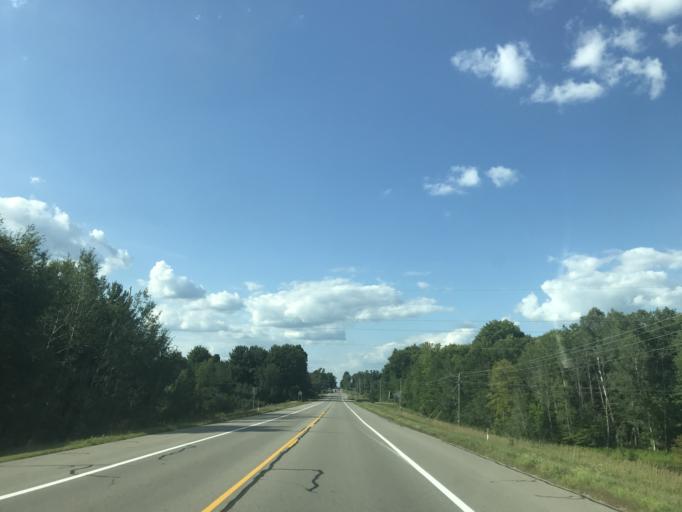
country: US
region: Michigan
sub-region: Newaygo County
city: White Cloud
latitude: 43.5641
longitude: -85.7715
